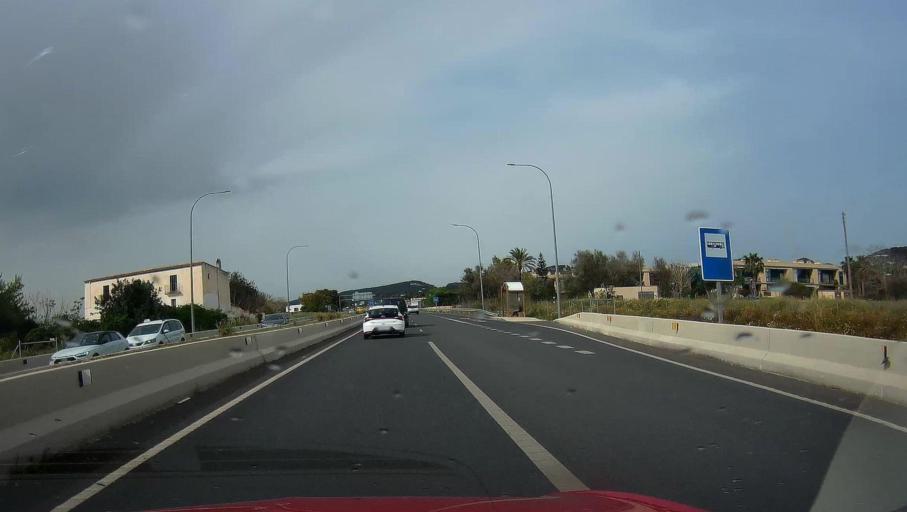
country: ES
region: Balearic Islands
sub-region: Illes Balears
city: Ibiza
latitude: 38.9284
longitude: 1.4423
